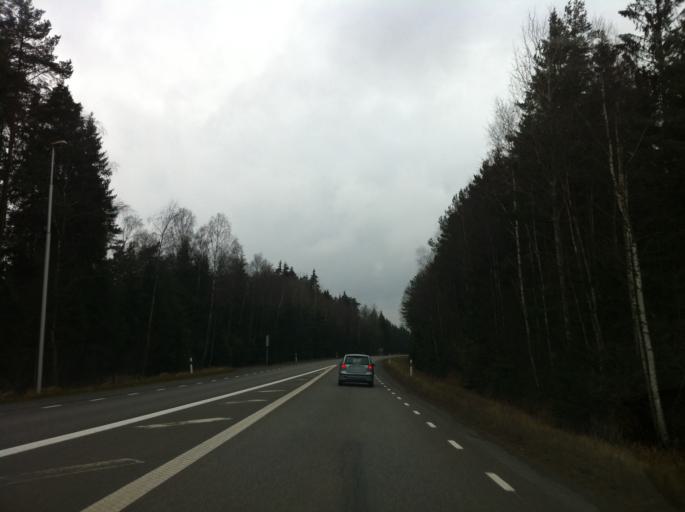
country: SE
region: Joenkoeping
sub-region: Vetlanda Kommun
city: Vetlanda
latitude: 57.4102
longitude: 14.9920
